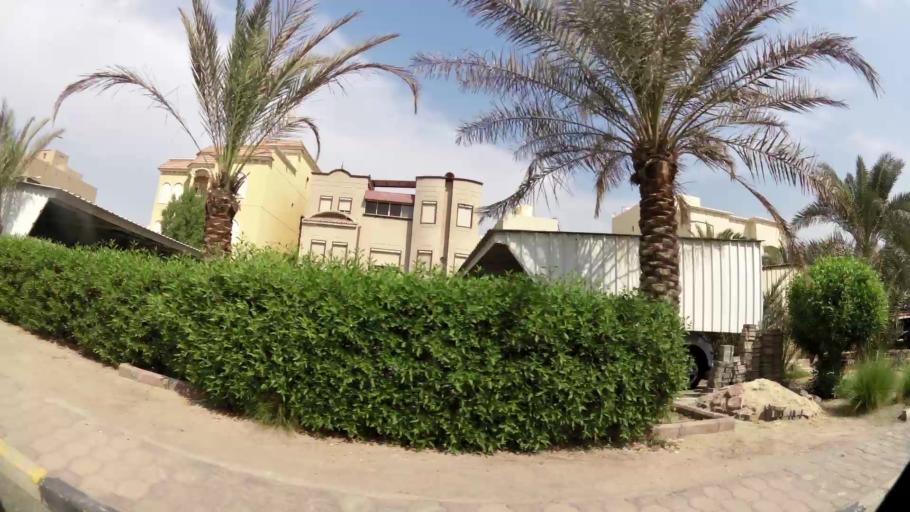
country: KW
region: Al Farwaniyah
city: Janub as Surrah
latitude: 29.2796
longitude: 48.0150
